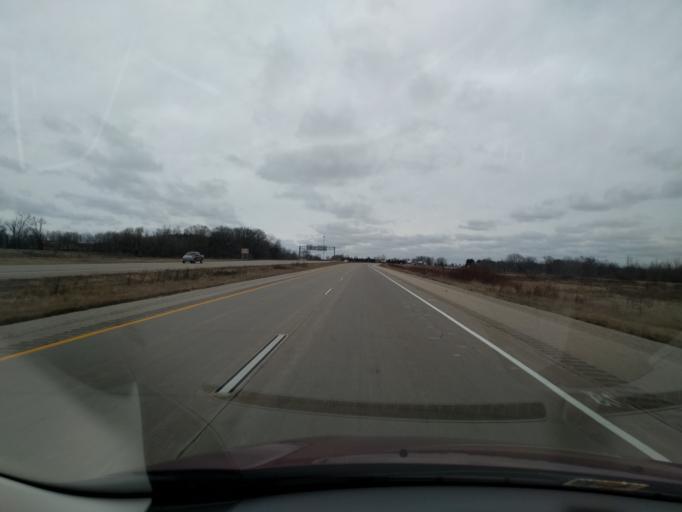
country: US
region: Wisconsin
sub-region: Winnebago County
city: Winneconne
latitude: 44.2341
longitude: -88.7353
